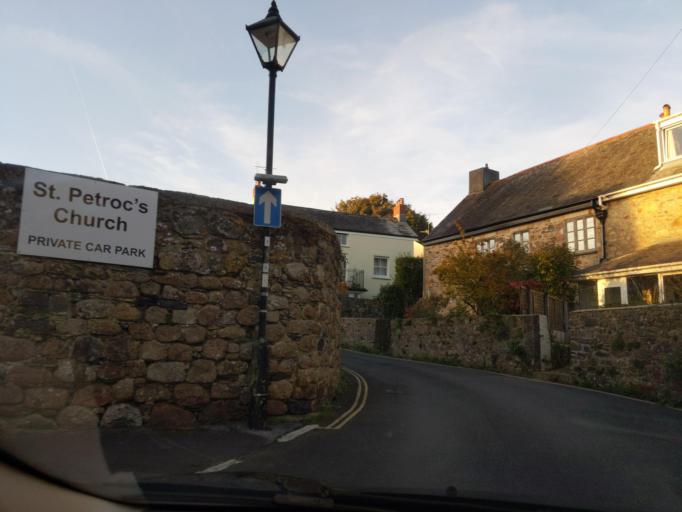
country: GB
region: England
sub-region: Devon
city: South Brent
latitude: 50.4275
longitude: -3.8363
